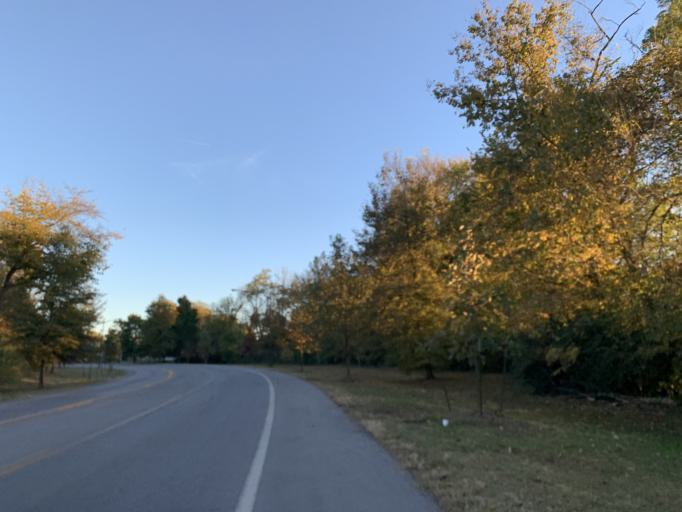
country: US
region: Kentucky
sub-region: Jefferson County
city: Shively
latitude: 38.2270
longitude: -85.8275
